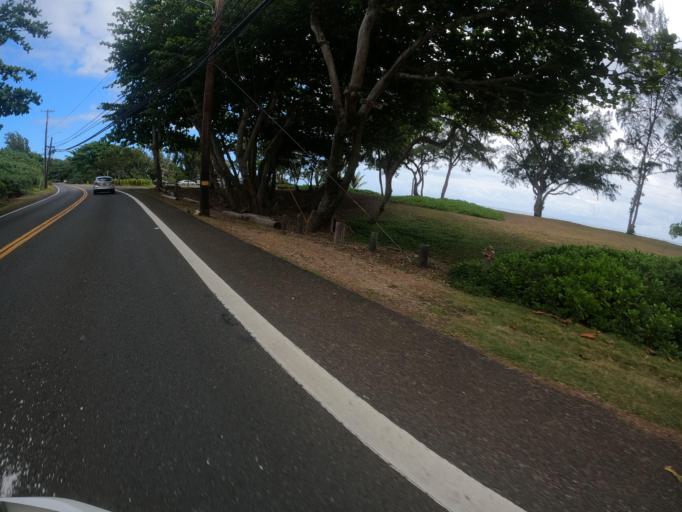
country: US
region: Hawaii
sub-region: Honolulu County
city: La'ie
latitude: 21.6314
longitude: -157.9215
